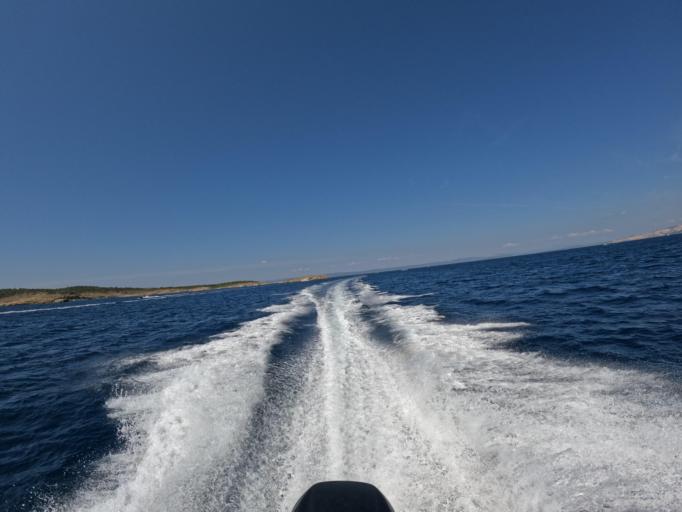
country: HR
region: Primorsko-Goranska
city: Lopar
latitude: 44.8528
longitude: 14.7386
